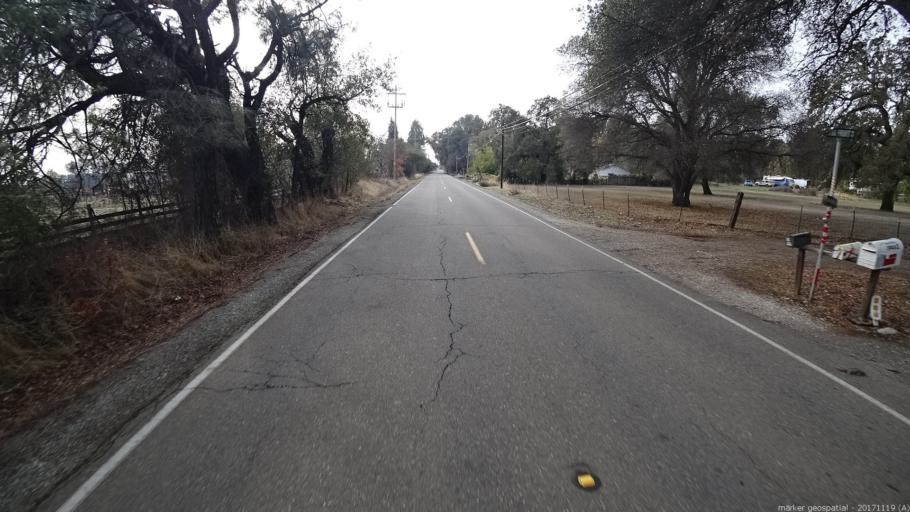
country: US
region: California
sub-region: Shasta County
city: Redding
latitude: 40.5264
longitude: -122.3337
